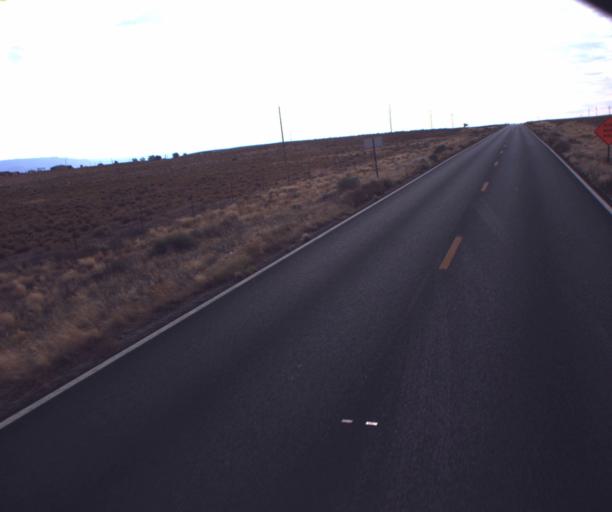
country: US
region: Arizona
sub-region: Apache County
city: Many Farms
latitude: 36.5919
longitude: -109.5631
